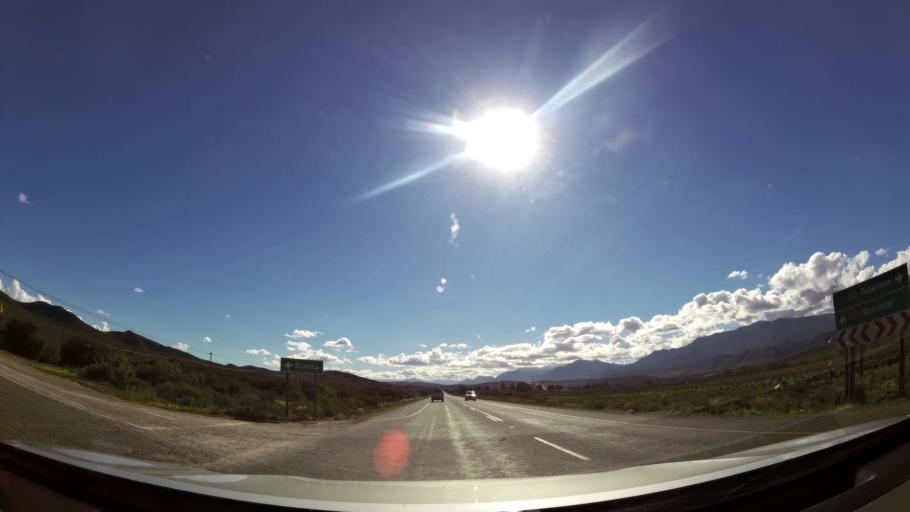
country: ZA
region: Western Cape
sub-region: Cape Winelands District Municipality
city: Ashton
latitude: -33.7699
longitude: 19.7493
